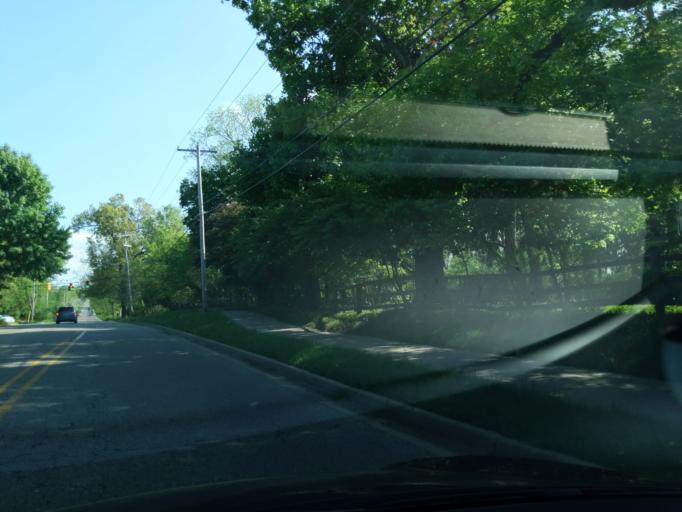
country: US
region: Michigan
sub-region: Ingham County
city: Okemos
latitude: 42.7056
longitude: -84.4104
